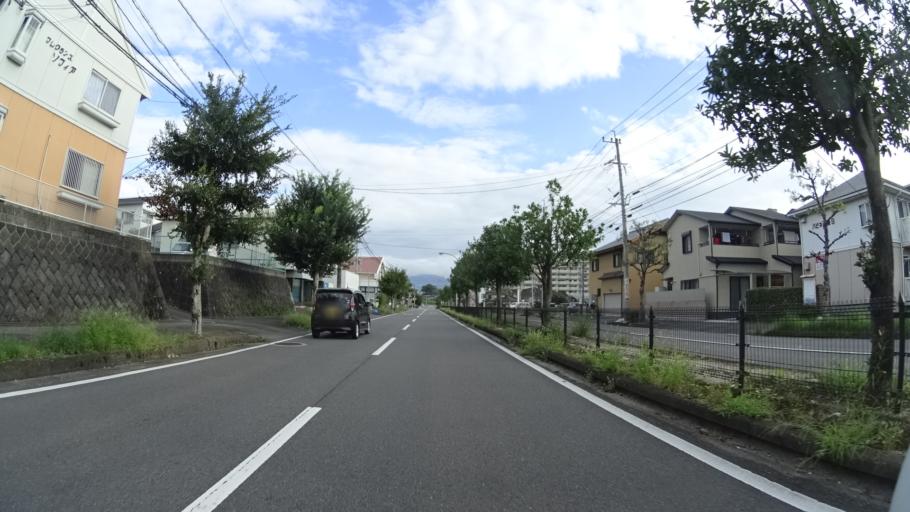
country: JP
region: Oita
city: Beppu
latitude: 33.3026
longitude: 131.4949
